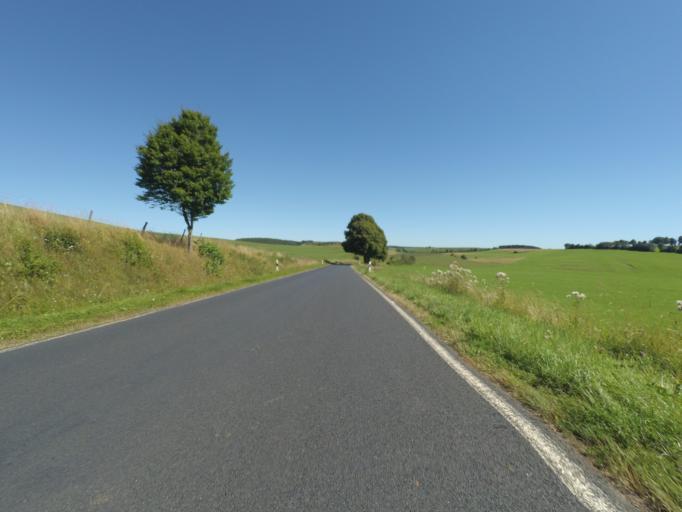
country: DE
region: Rheinland-Pfalz
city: Feusdorf
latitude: 50.3464
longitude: 6.6232
